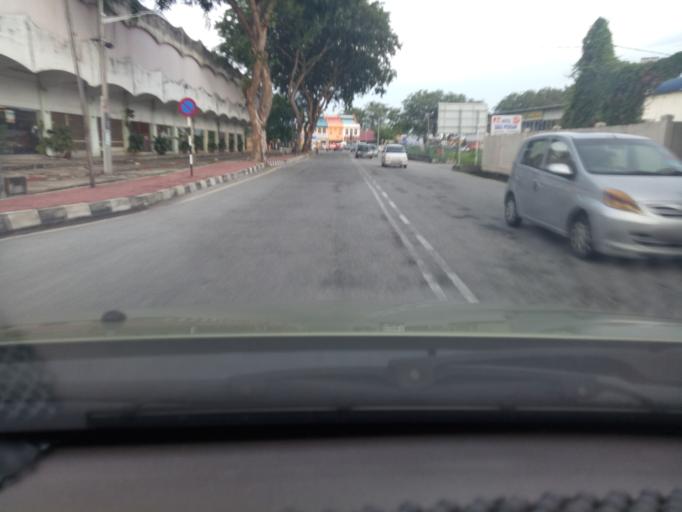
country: MY
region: Kedah
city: Alor Setar
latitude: 6.1135
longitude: 100.3634
